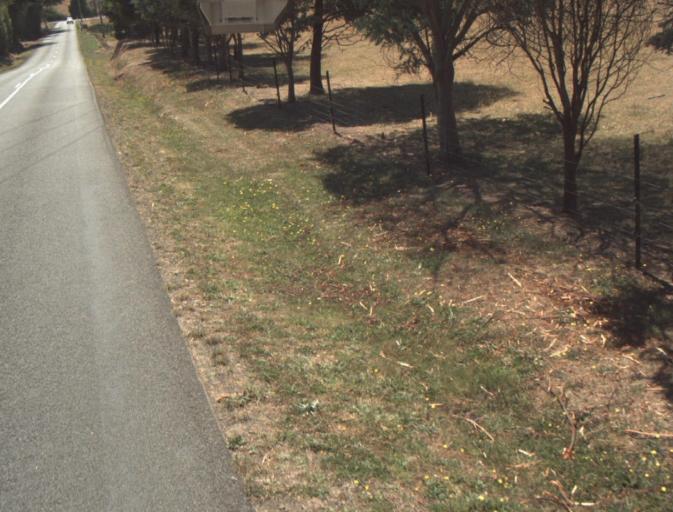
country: AU
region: Tasmania
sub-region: Launceston
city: Mayfield
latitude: -41.2623
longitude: 147.1353
